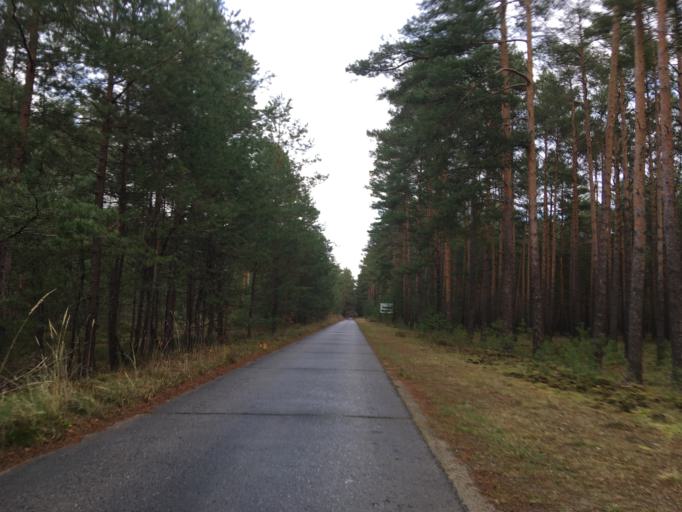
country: DE
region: Brandenburg
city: Tauer
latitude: 51.9590
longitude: 14.5270
